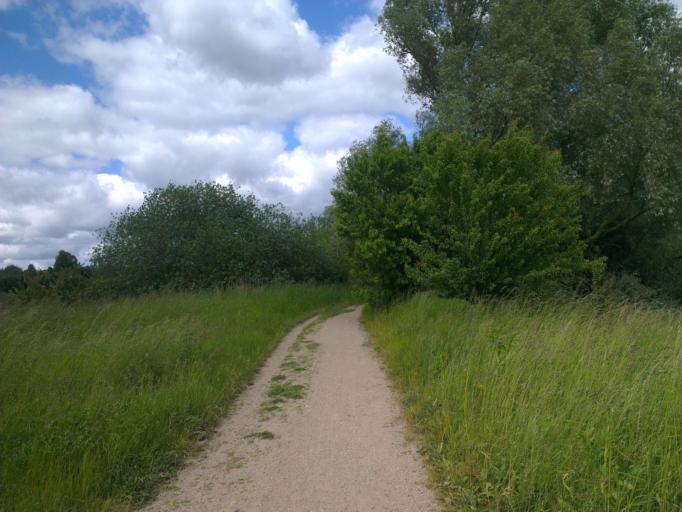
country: DK
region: Capital Region
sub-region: Frederikssund Kommune
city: Slangerup
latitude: 55.8499
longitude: 12.1907
